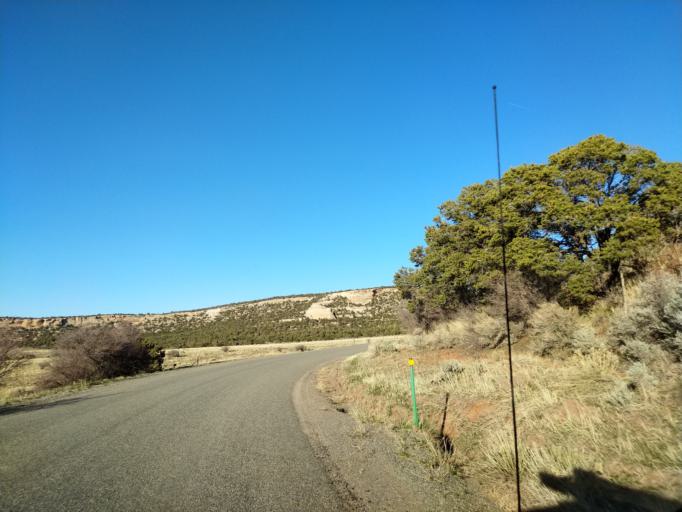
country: US
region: Colorado
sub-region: Mesa County
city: Loma
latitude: 38.9605
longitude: -109.0113
